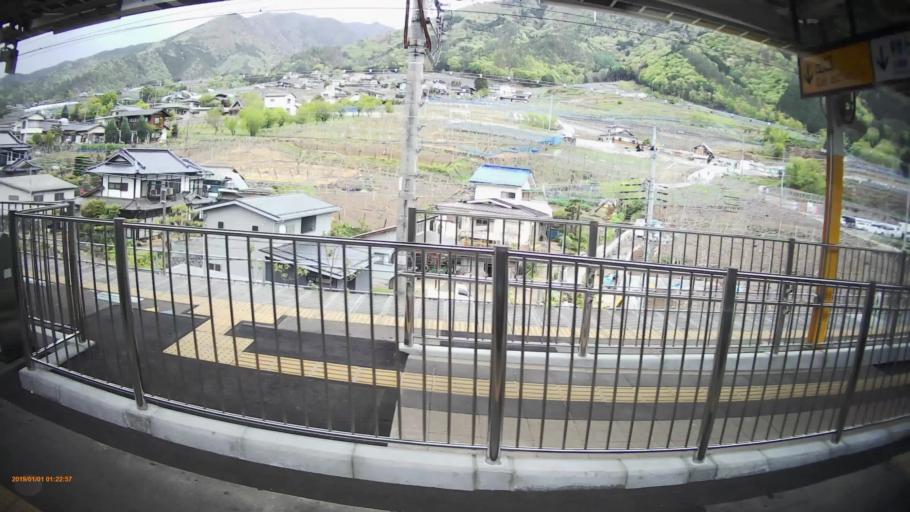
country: JP
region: Yamanashi
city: Enzan
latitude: 35.6726
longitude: 138.7433
